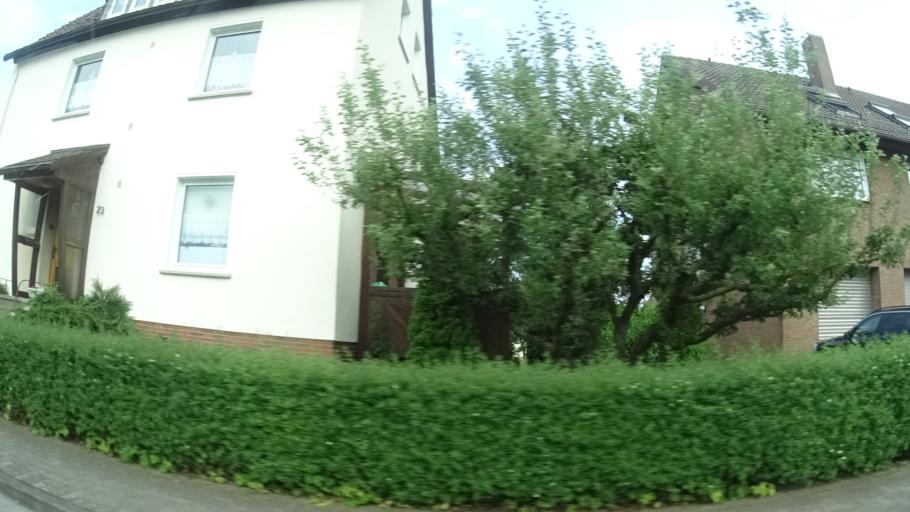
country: DE
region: Hesse
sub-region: Regierungsbezirk Kassel
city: Bad Arolsen
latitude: 51.3802
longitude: 9.0560
